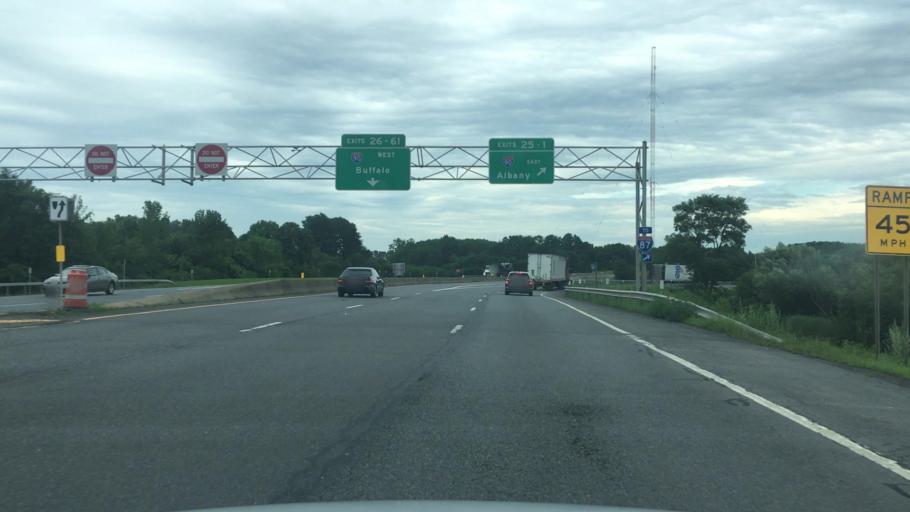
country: US
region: New York
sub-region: Schenectady County
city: Rotterdam
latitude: 42.7888
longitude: -74.0200
